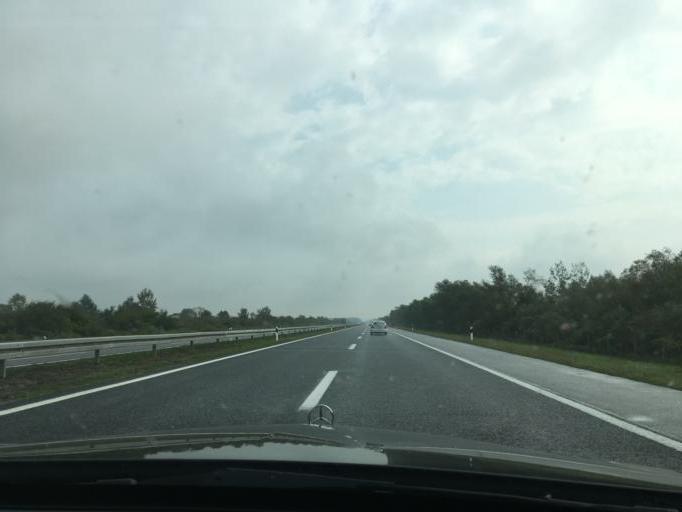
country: HR
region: Brodsko-Posavska
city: Oriovac
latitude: 45.1521
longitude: 17.7894
